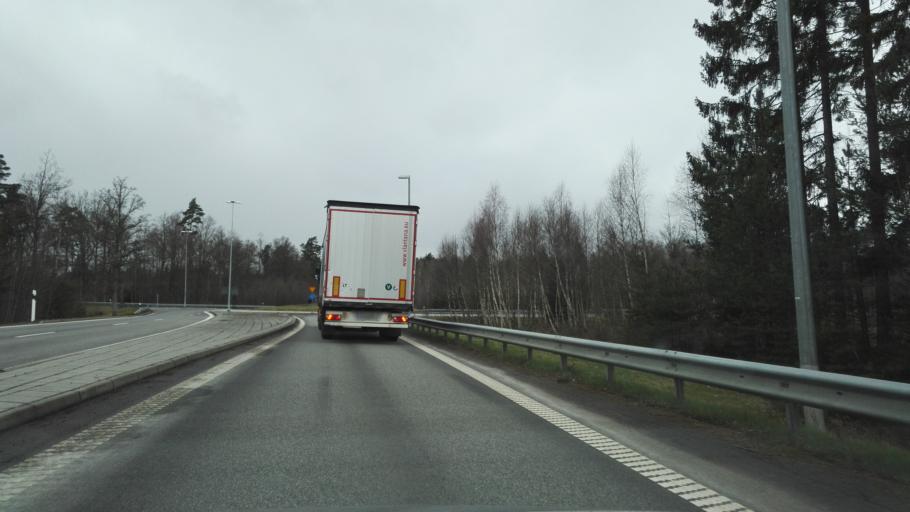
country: SE
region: Skane
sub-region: Osby Kommun
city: Osby
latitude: 56.3681
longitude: 14.0274
